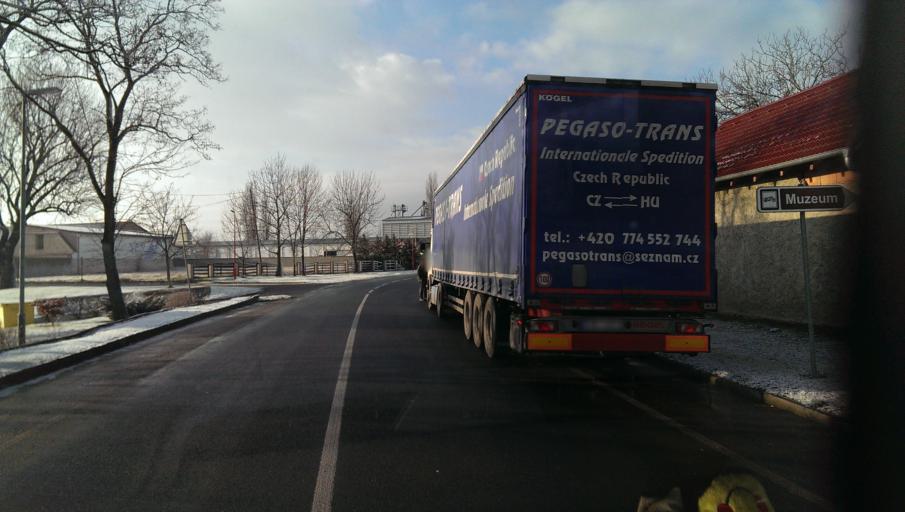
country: CZ
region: Ustecky
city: Budyne nad Ohri
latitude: 50.4124
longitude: 14.0909
